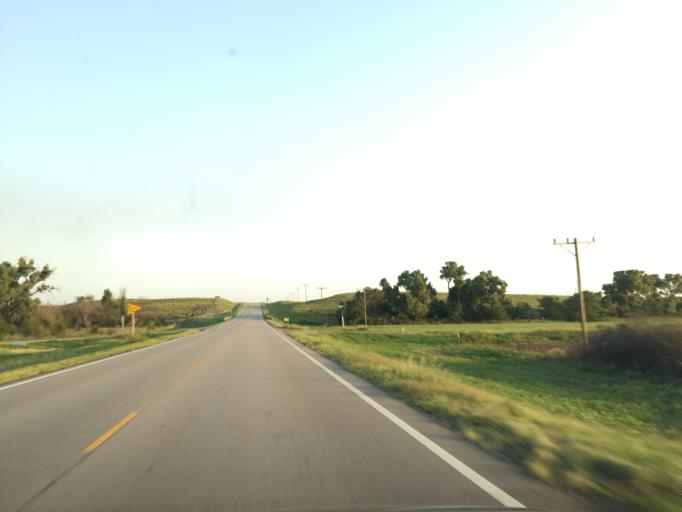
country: US
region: Kansas
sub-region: Ellsworth County
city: Ellsworth
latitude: 38.6828
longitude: -98.2022
